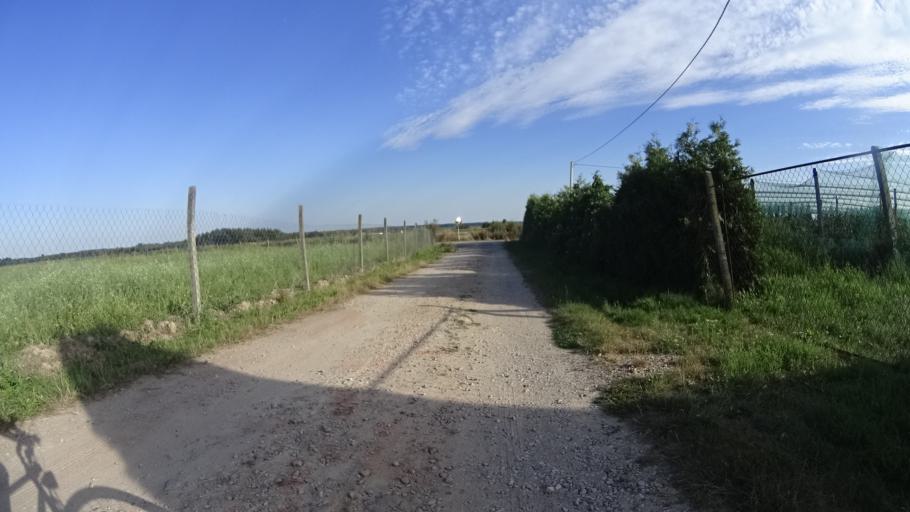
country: PL
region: Masovian Voivodeship
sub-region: Powiat bialobrzeski
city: Wysmierzyce
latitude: 51.6775
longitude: 20.8183
